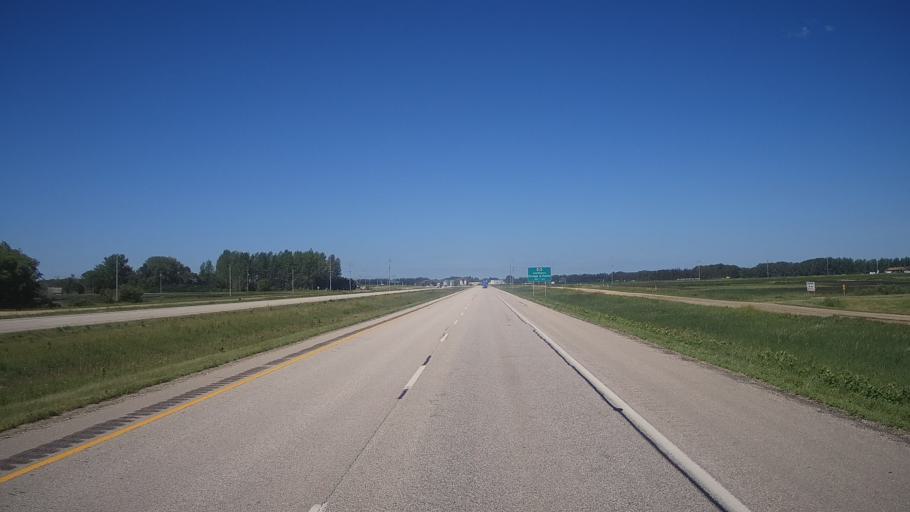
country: CA
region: Manitoba
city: Portage la Prairie
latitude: 49.9598
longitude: -98.2517
